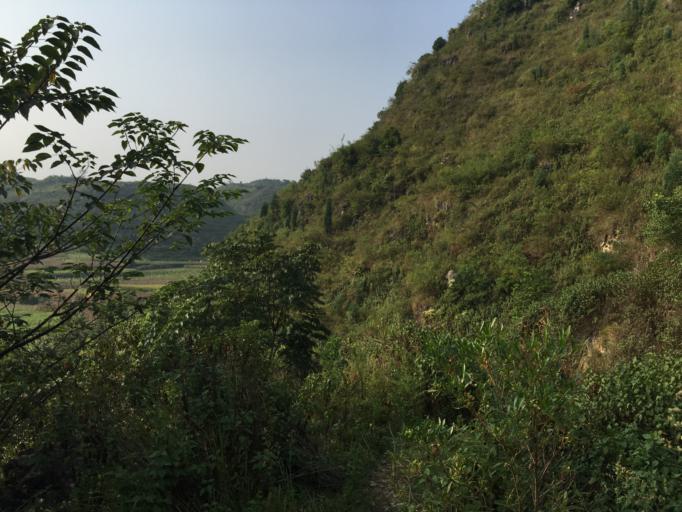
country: CN
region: Guangxi Zhuangzu Zizhiqu
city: Xinzhou
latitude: 25.4398
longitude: 105.6370
